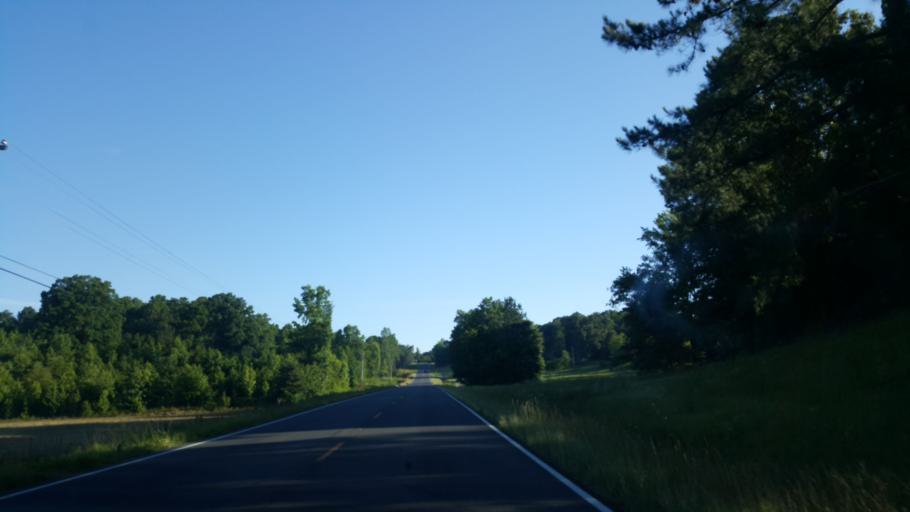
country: US
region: Tennessee
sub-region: Henderson County
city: Lexington
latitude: 35.5822
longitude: -88.3893
